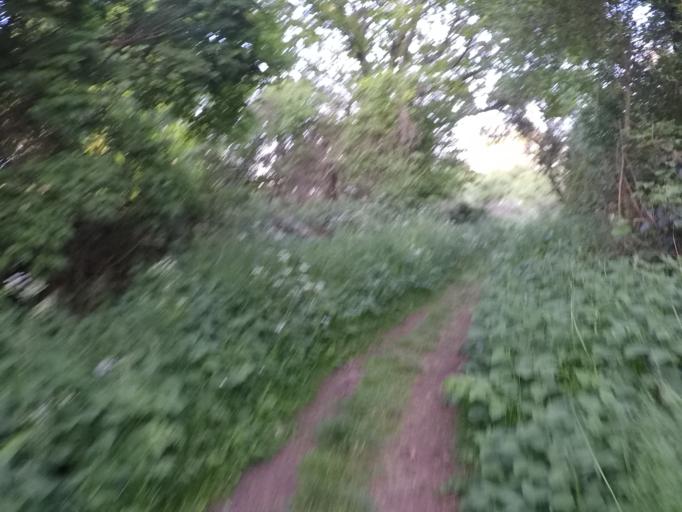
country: GB
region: England
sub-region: Oxfordshire
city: Charlbury
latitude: 51.8291
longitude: -1.5062
